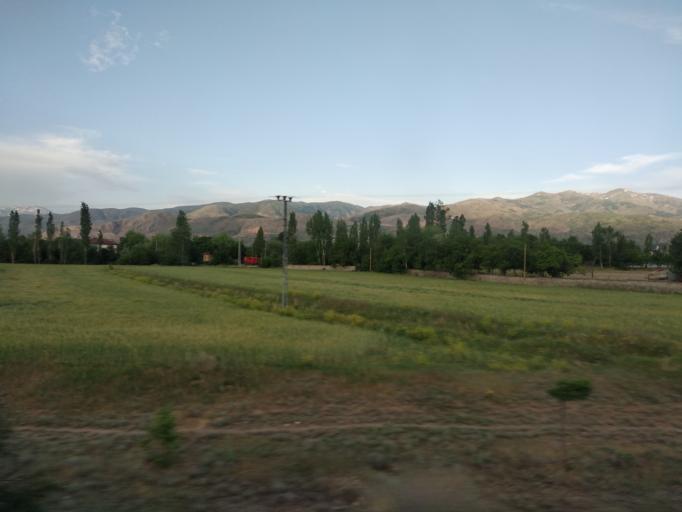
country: TR
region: Erzincan
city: Catalarmut
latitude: 39.8065
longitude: 39.3663
